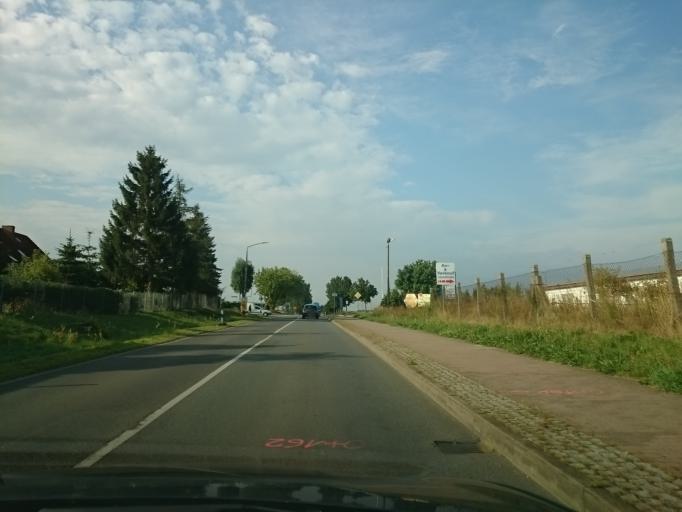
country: DE
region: Mecklenburg-Vorpommern
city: Demmin
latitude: 53.8911
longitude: 13.0337
